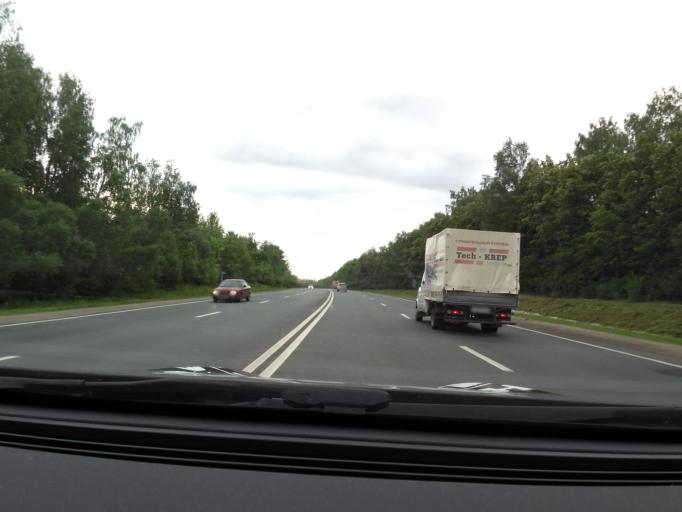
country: RU
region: Chuvashia
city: Tsivil'sk
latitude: 55.9078
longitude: 47.4256
